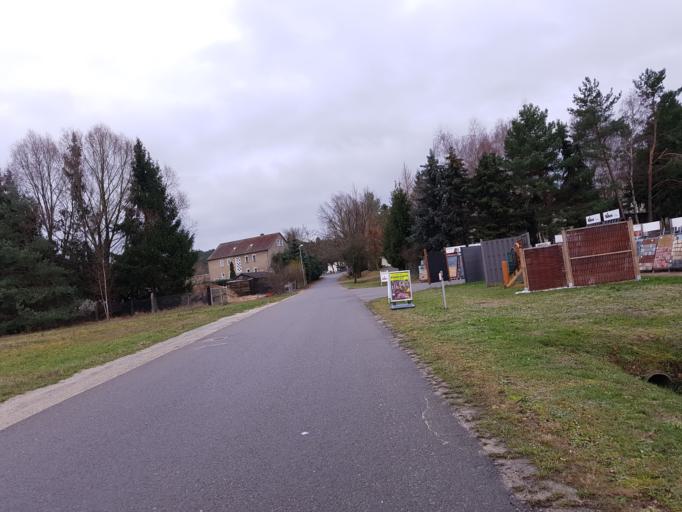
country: DE
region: Brandenburg
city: Groden
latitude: 51.4021
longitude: 13.5649
